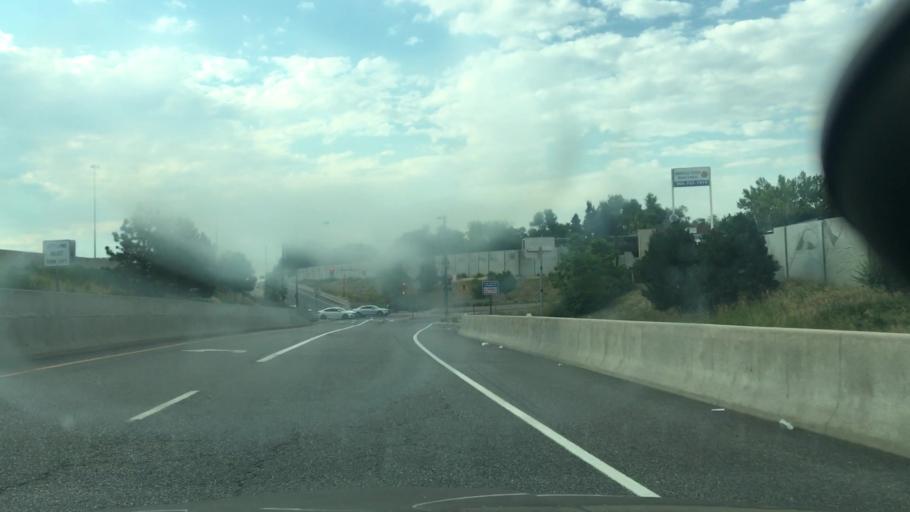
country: US
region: Colorado
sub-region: Arapahoe County
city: Glendale
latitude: 39.6667
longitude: -104.9246
